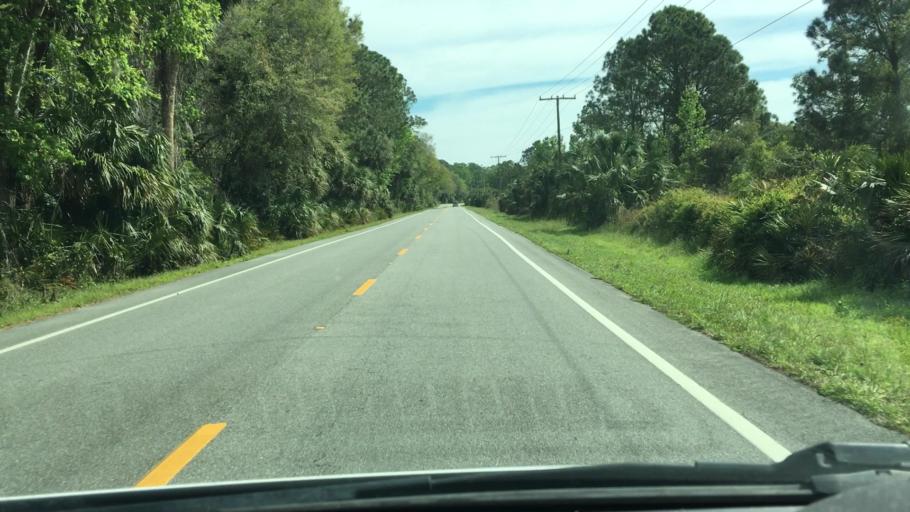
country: US
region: Florida
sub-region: Lake County
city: Lake Mack-Forest Hills
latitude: 29.0097
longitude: -81.3992
